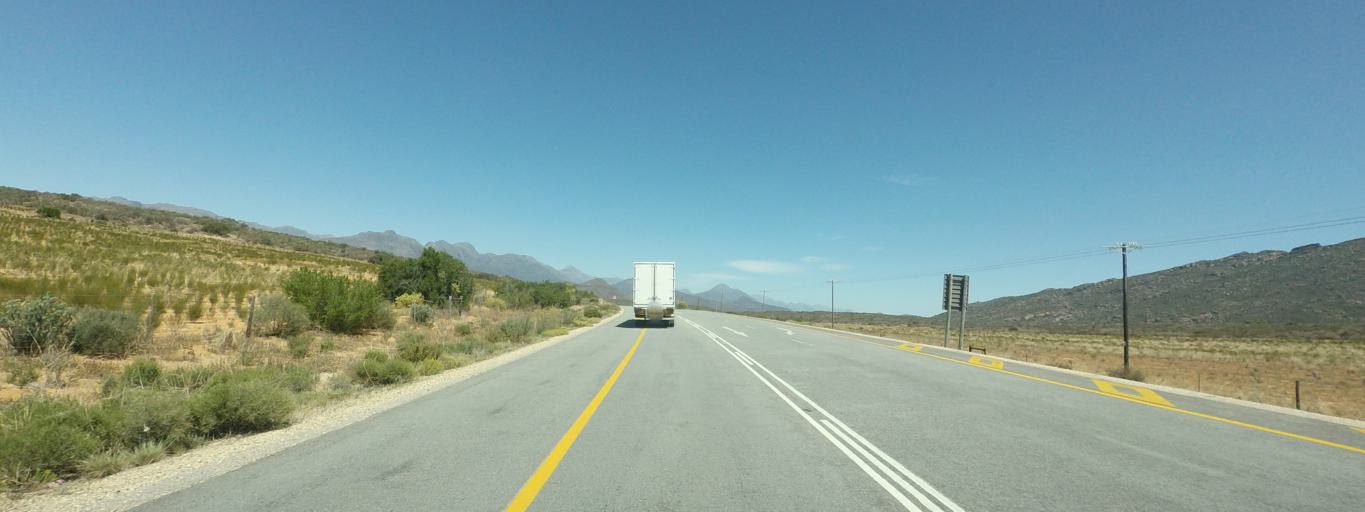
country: ZA
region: Western Cape
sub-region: West Coast District Municipality
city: Clanwilliam
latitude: -32.3199
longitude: 18.9139
